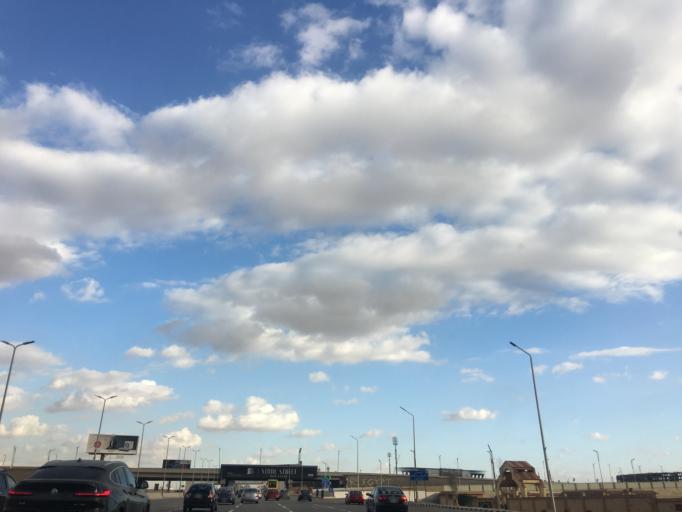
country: EG
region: Muhafazat al Qahirah
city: Cairo
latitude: 30.0232
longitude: 31.3668
